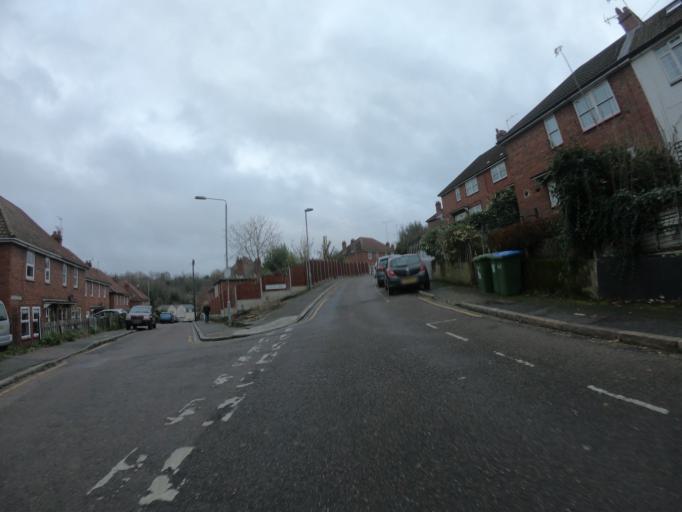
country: GB
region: England
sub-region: Greater London
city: Woolwich
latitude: 51.4872
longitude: 0.0398
